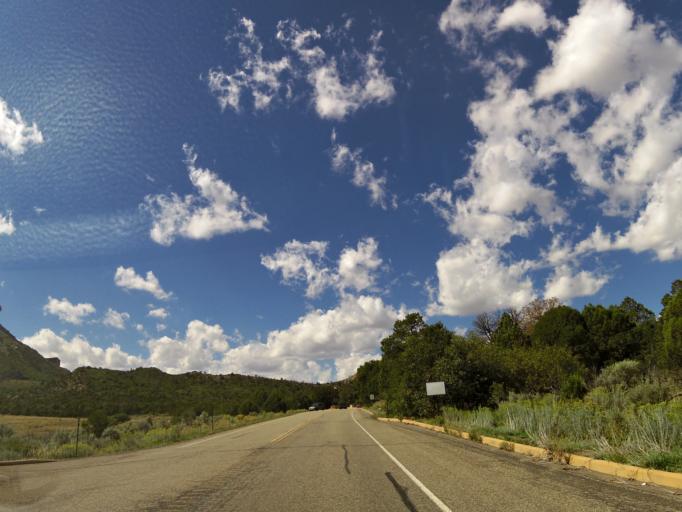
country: US
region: Colorado
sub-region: Montezuma County
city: Mancos
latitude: 37.3327
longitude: -108.4139
